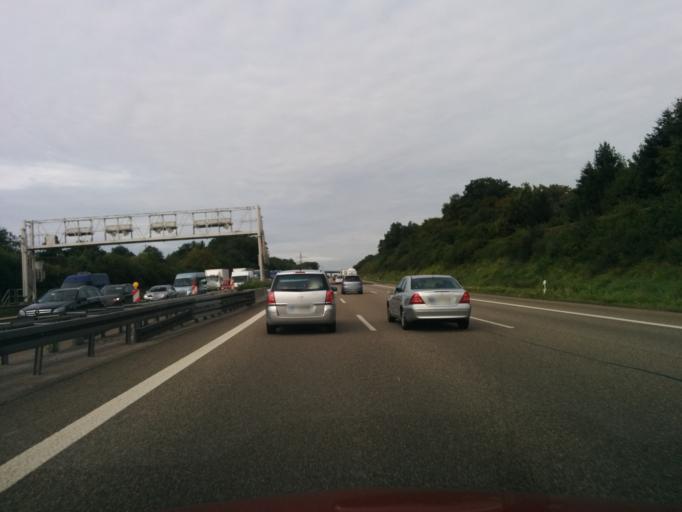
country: DE
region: Baden-Wuerttemberg
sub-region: Karlsruhe Region
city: Ispringen
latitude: 48.9082
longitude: 8.6792
